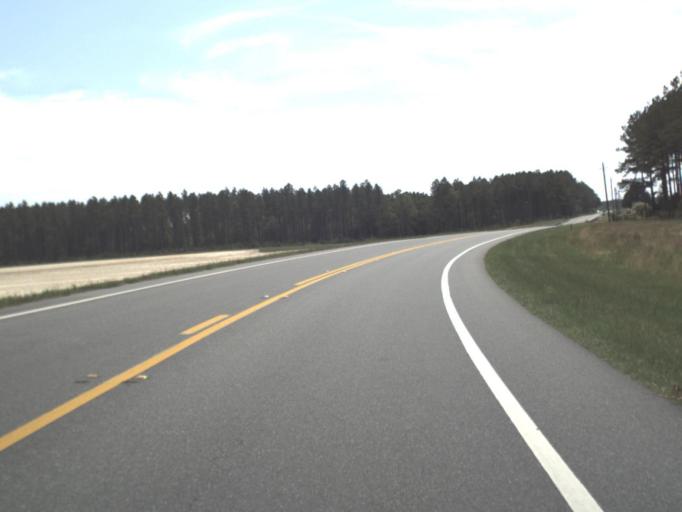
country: US
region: Florida
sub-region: Gulf County
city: Wewahitchka
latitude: 30.2188
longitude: -85.2048
